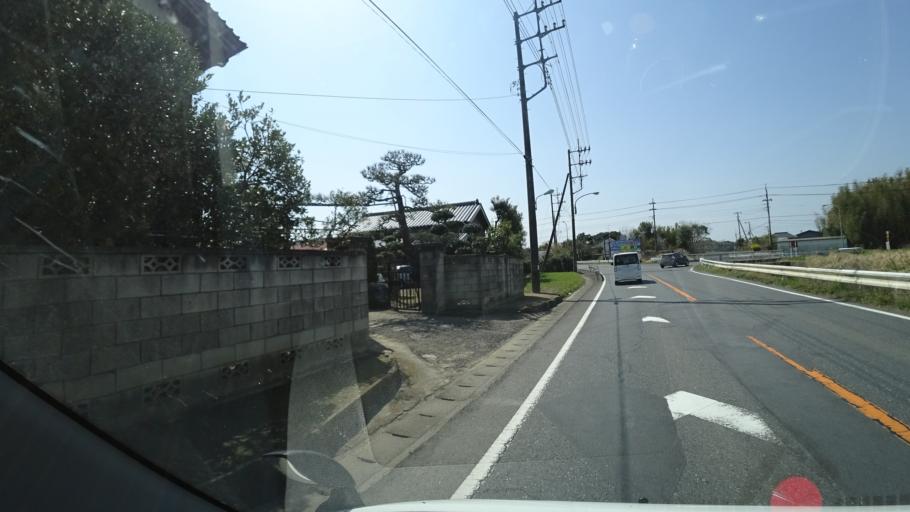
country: JP
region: Chiba
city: Narita
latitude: 35.8637
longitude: 140.2852
